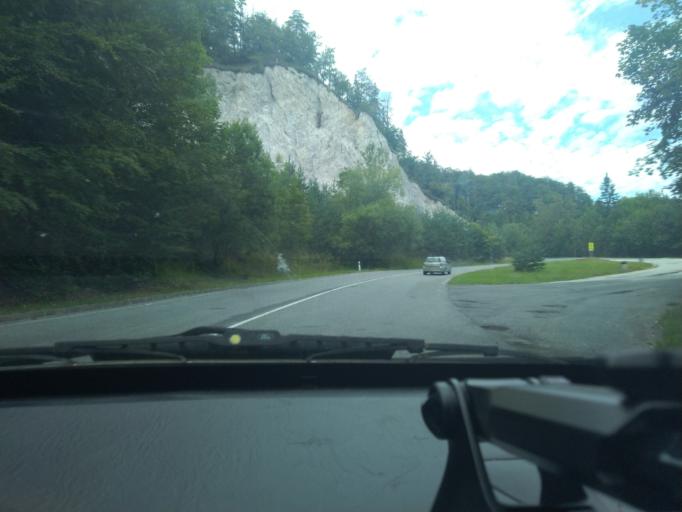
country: SK
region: Banskobystricky
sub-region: Okres Ziar nad Hronom
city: Kremnica
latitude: 48.8263
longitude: 19.0190
